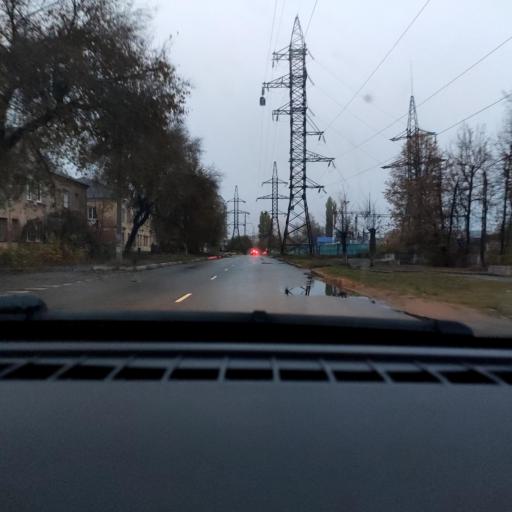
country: RU
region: Voronezj
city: Voronezh
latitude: 51.6946
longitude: 39.2084
